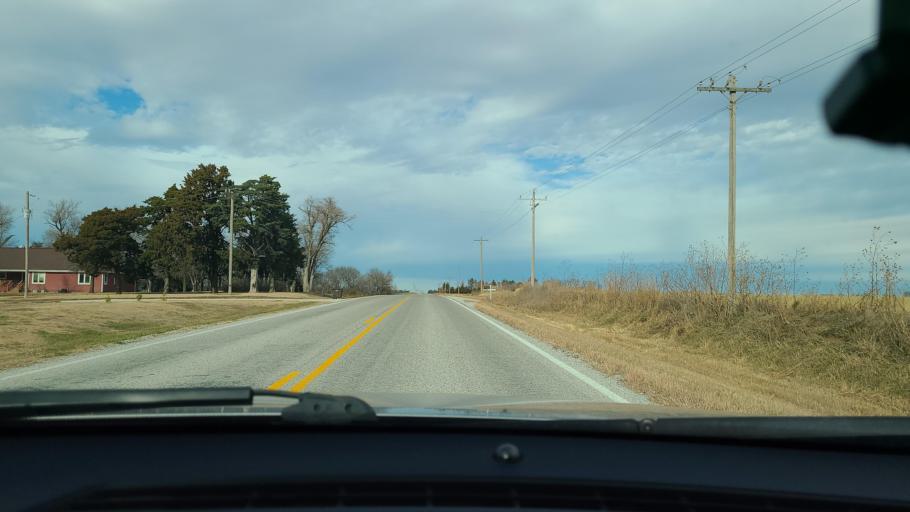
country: US
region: Kansas
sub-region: McPherson County
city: Inman
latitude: 38.2944
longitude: -97.9250
